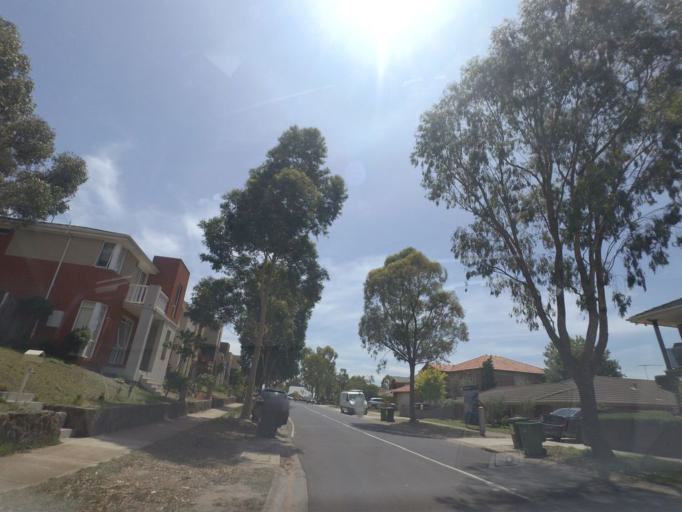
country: AU
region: Victoria
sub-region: Hume
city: Roxburgh Park
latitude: -37.6346
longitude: 144.9182
